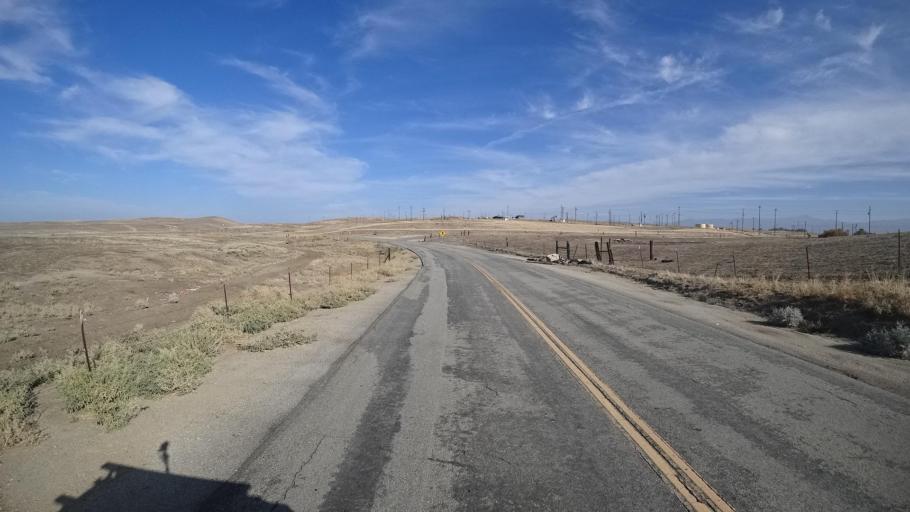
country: US
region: California
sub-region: Kern County
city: Oildale
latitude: 35.6244
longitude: -118.9879
